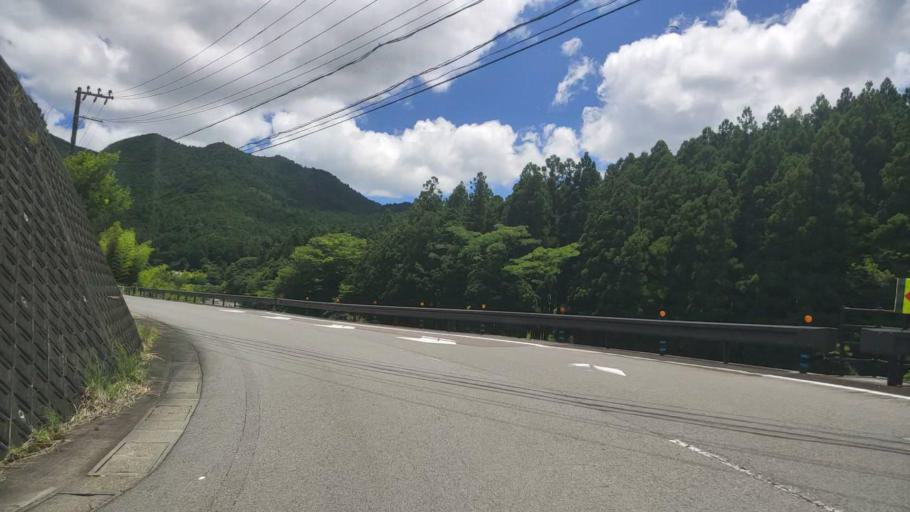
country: JP
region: Mie
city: Owase
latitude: 33.9585
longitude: 136.0645
